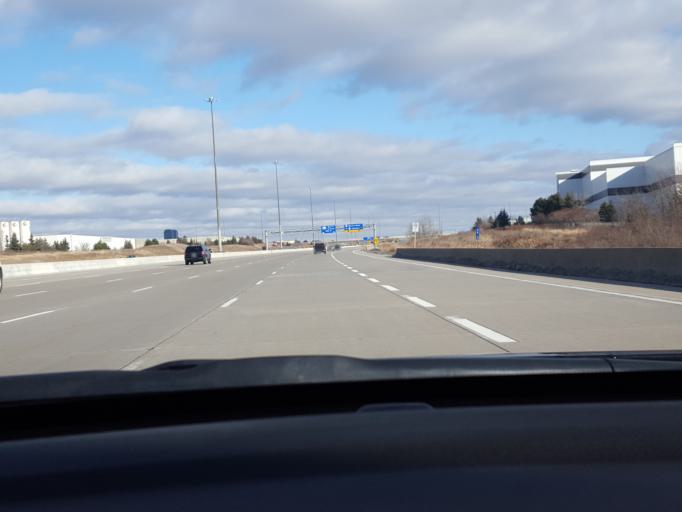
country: CA
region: Ontario
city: Concord
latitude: 43.7776
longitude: -79.5606
